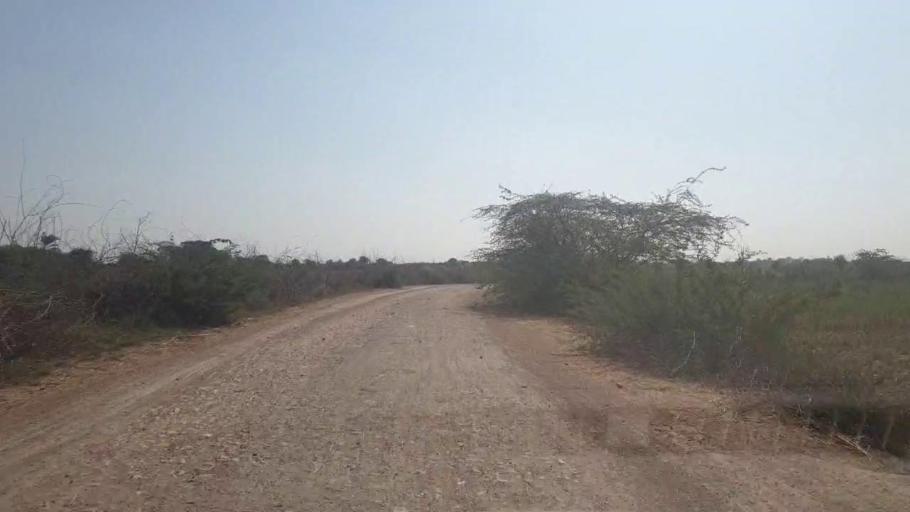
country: PK
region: Sindh
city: Badin
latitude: 24.5966
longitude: 68.8540
